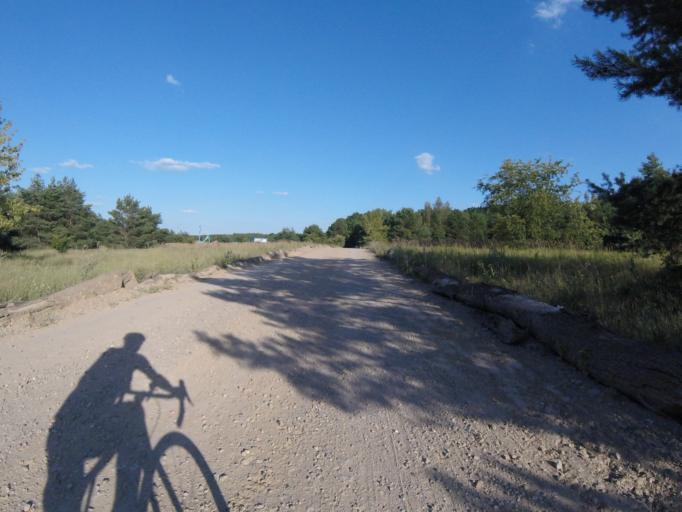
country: DE
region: Brandenburg
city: Zossen
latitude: 52.1978
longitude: 13.5071
